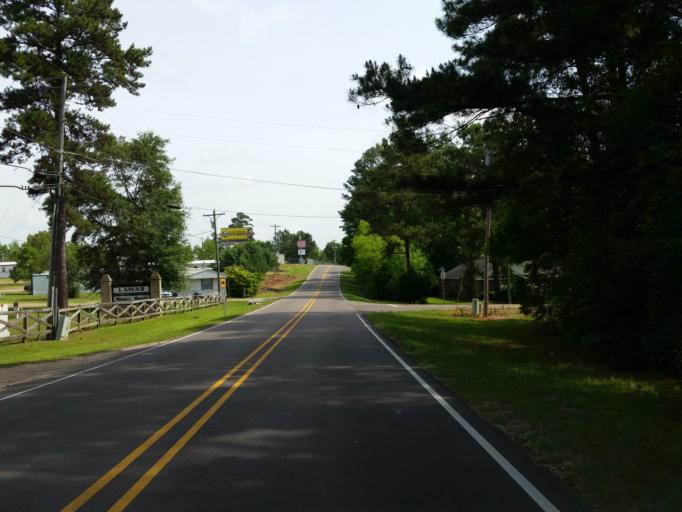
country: US
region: Mississippi
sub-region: Lamar County
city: West Hattiesburg
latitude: 31.3094
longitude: -89.3722
